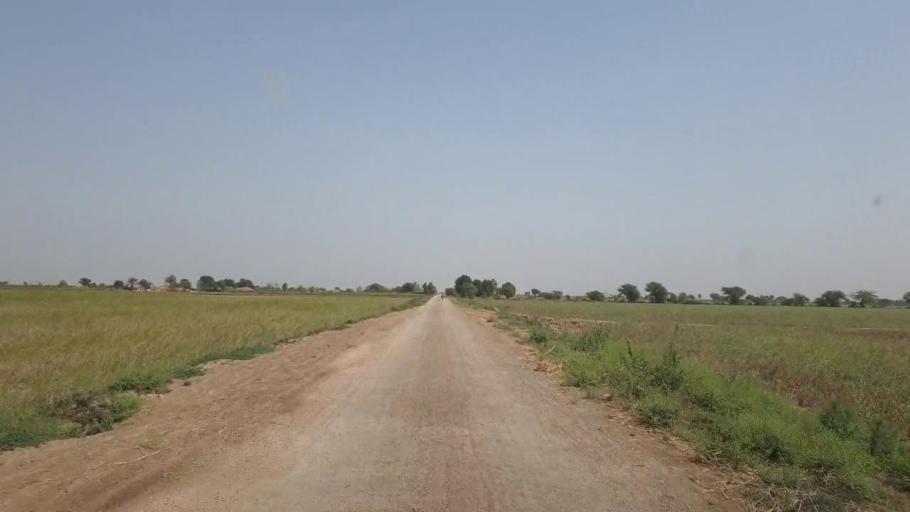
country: PK
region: Sindh
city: Badin
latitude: 24.4774
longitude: 68.5696
